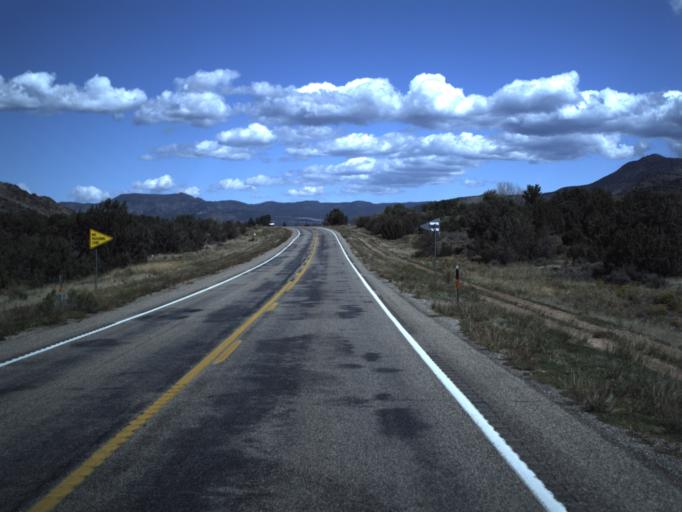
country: US
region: Utah
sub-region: Washington County
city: Ivins
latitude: 37.3608
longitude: -113.6725
